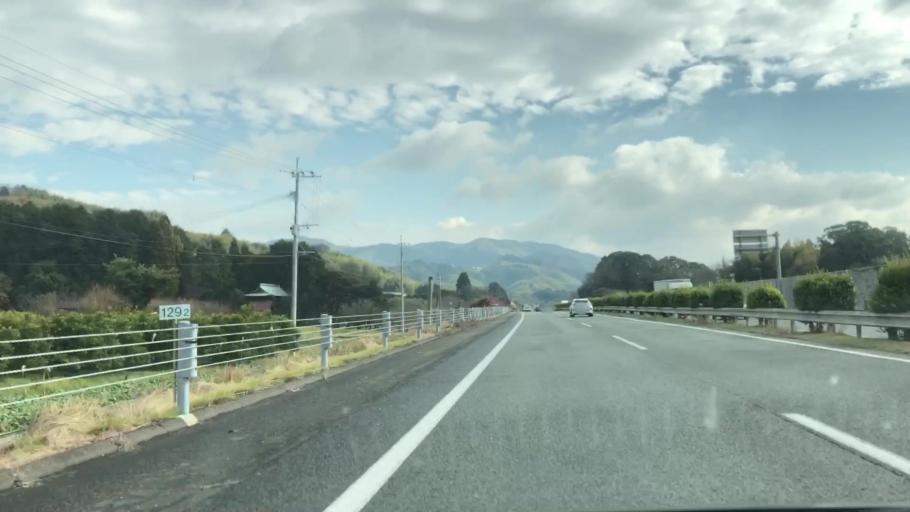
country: JP
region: Fukuoka
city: Setakamachi-takayanagi
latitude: 33.1196
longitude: 130.5230
